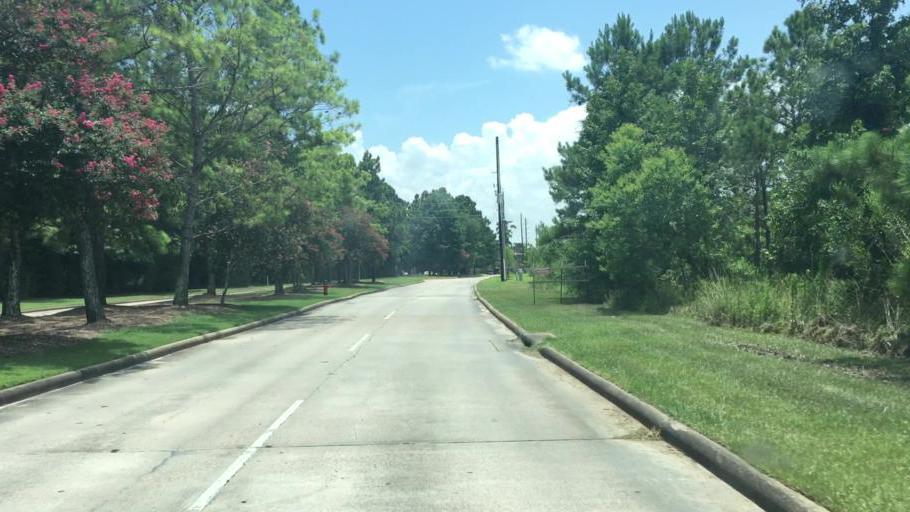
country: US
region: Texas
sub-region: Harris County
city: Atascocita
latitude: 29.9817
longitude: -95.1908
